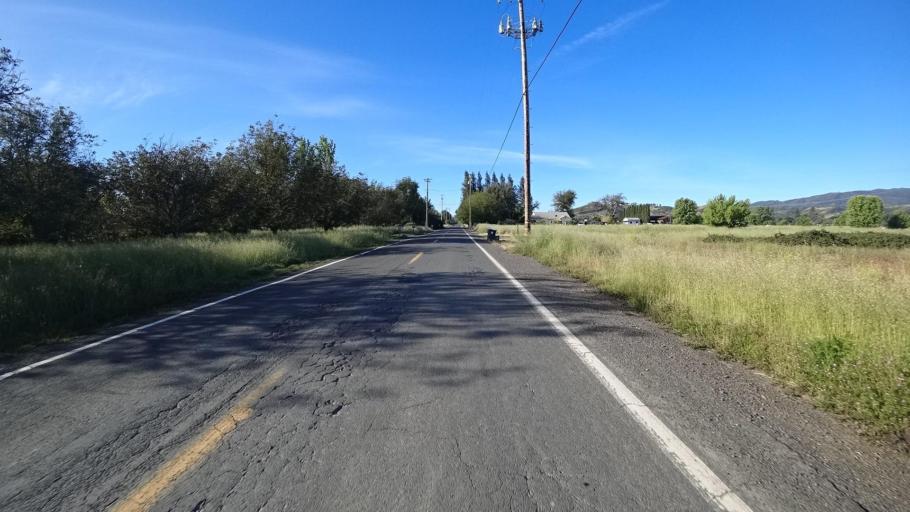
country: US
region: California
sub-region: Lake County
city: North Lakeport
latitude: 39.0785
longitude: -122.9498
